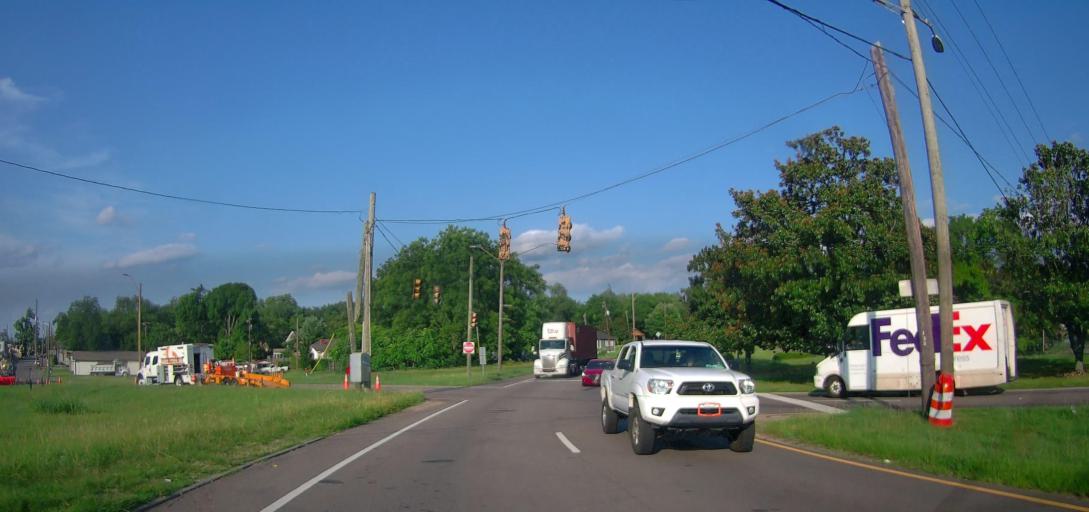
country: US
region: Alabama
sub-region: Jefferson County
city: Mountain Brook
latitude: 33.5280
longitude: -86.7610
